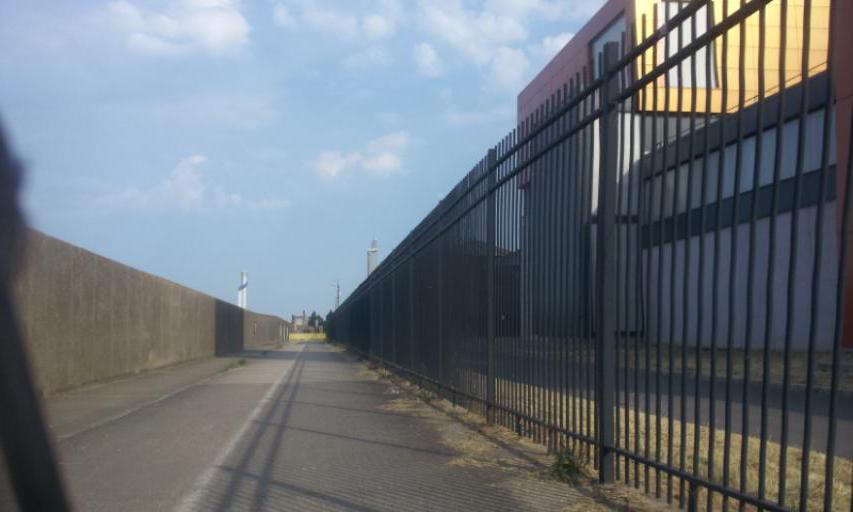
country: GB
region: England
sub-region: Greater London
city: Belvedere
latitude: 51.5086
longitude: 0.1415
